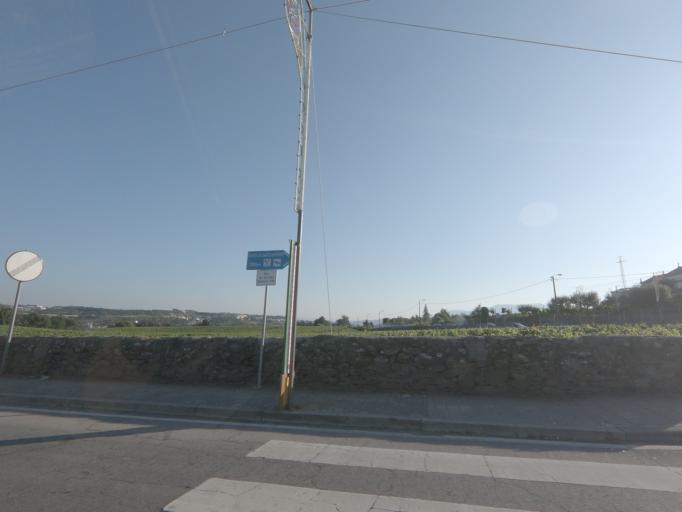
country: PT
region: Vila Real
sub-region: Vila Real
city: Vila Real
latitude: 41.2997
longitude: -7.7154
